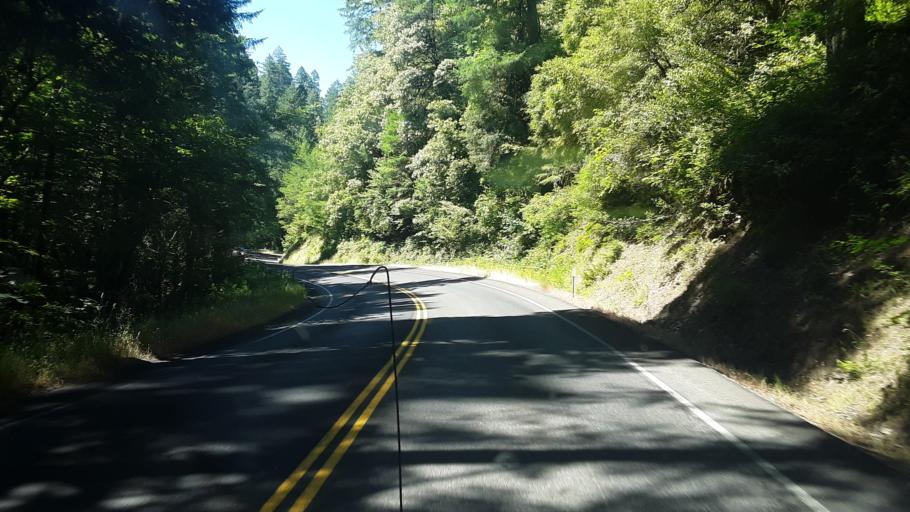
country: US
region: Oregon
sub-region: Josephine County
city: Cave Junction
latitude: 41.9299
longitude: -123.7568
